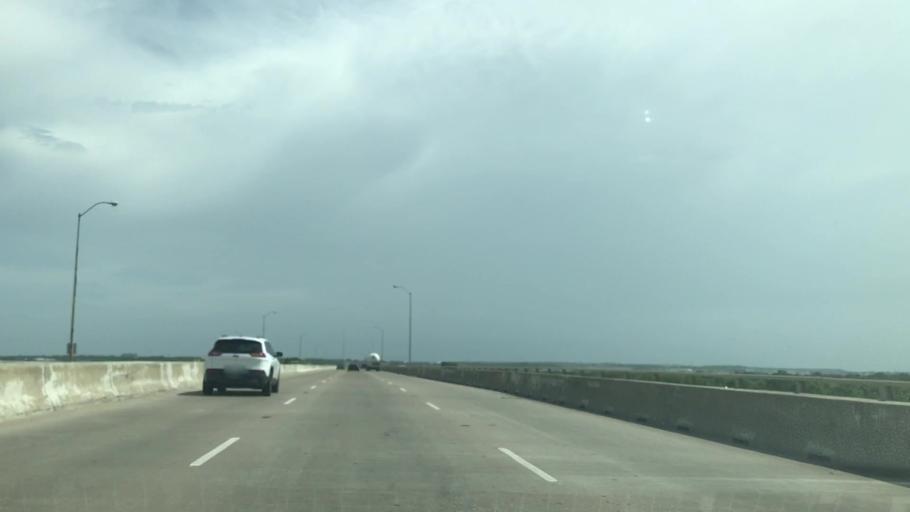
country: US
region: Texas
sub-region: Dallas County
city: Cockrell Hill
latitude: 32.8013
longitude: -96.8739
